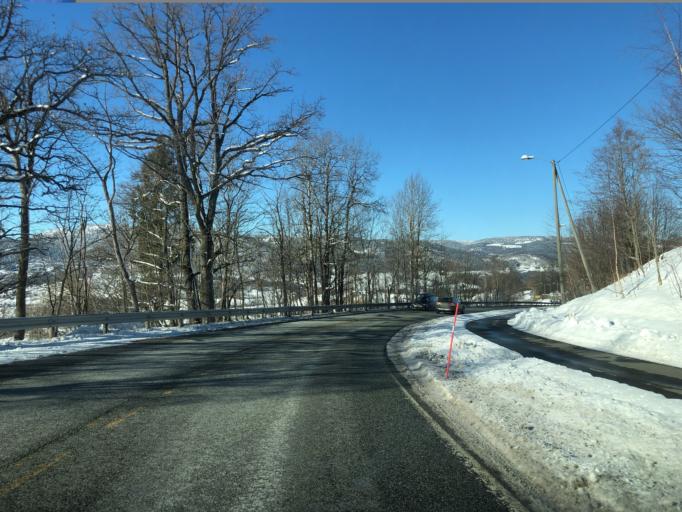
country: NO
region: Buskerud
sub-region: Lier
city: Tranby
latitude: 59.8115
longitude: 10.2539
